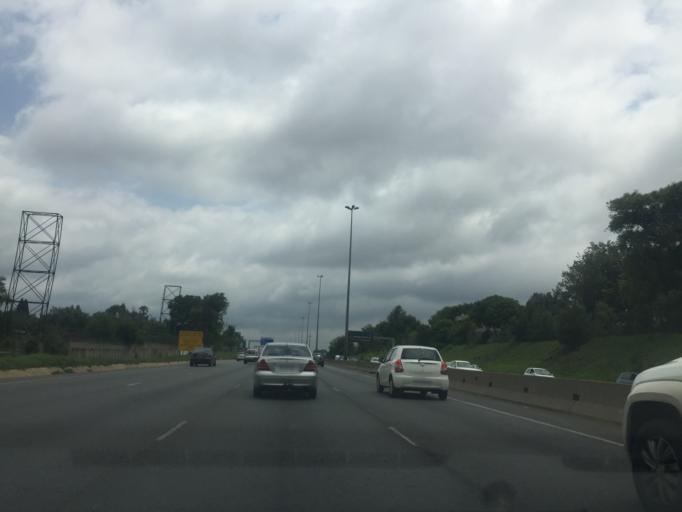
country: ZA
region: Gauteng
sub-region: City of Johannesburg Metropolitan Municipality
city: Johannesburg
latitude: -26.1186
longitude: 28.0736
